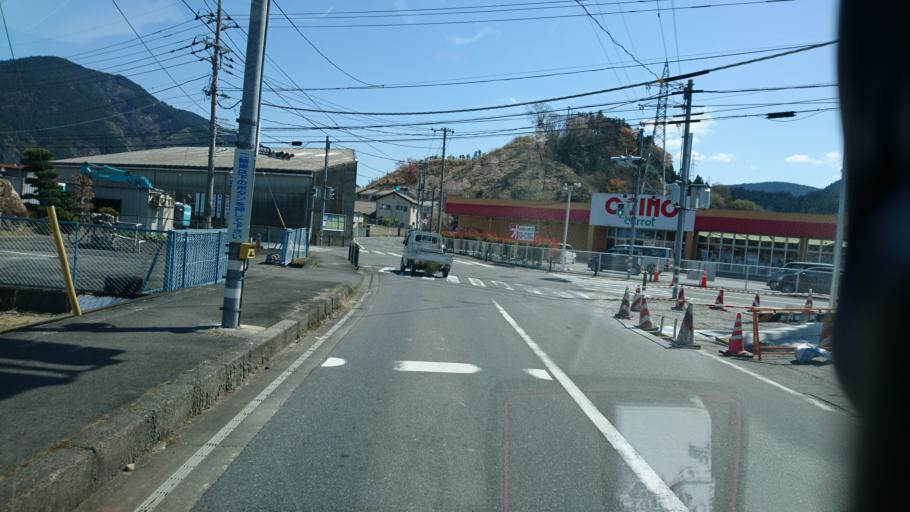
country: JP
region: Shizuoka
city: Fujinomiya
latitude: 35.2811
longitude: 138.4526
